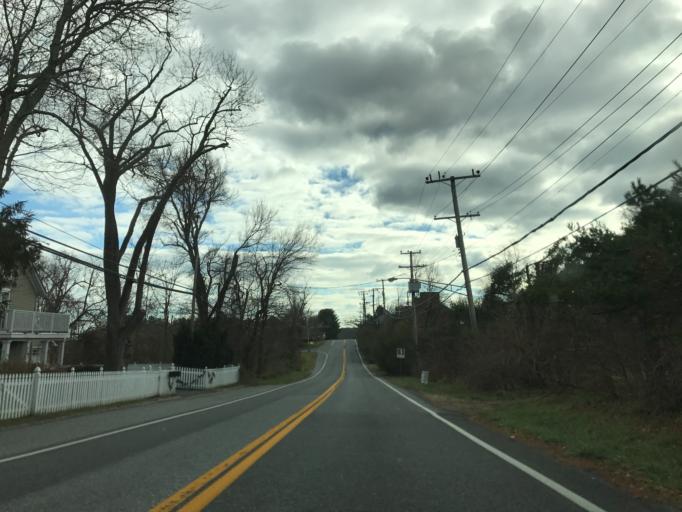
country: US
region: Pennsylvania
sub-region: York County
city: New Freedom
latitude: 39.6244
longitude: -76.6586
